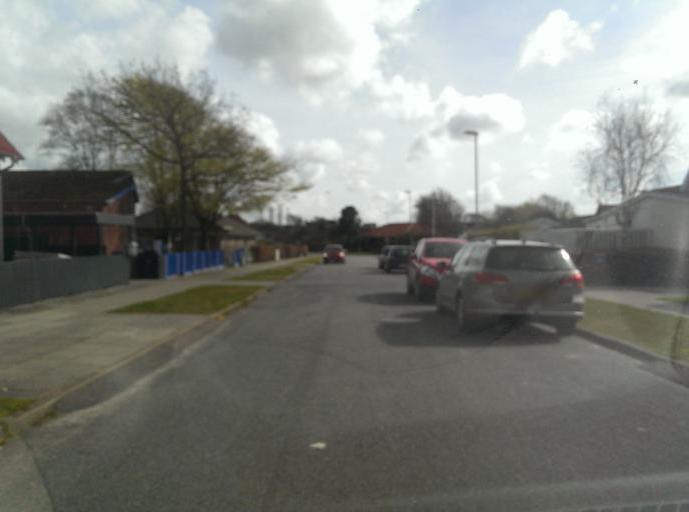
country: DK
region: South Denmark
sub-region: Esbjerg Kommune
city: Esbjerg
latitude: 55.4694
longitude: 8.4791
